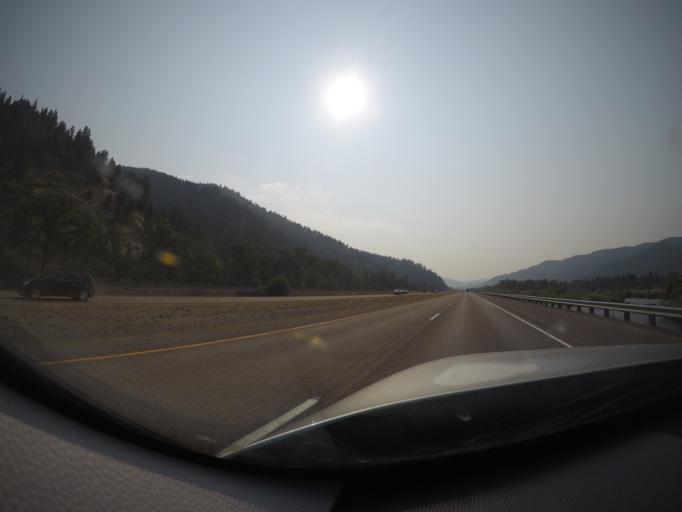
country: US
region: Montana
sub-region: Missoula County
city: Bonner-West Riverside
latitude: 46.8216
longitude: -113.8040
